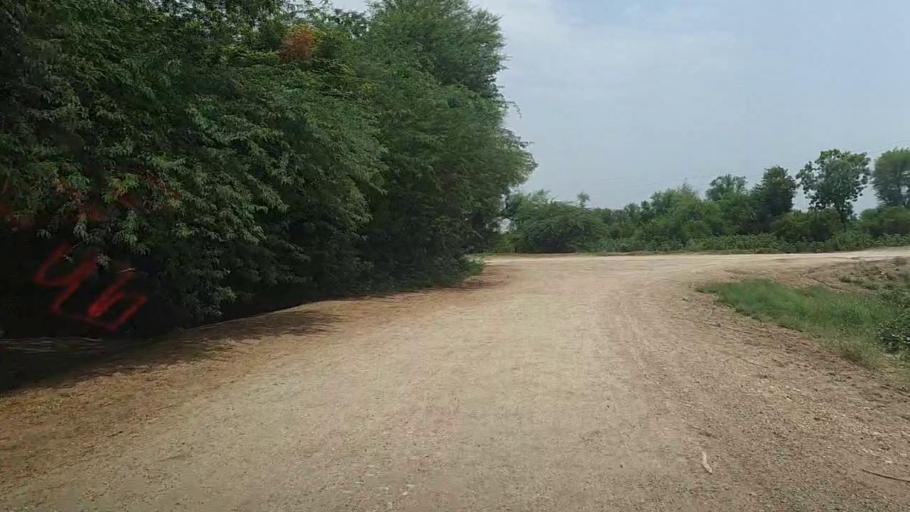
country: PK
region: Sindh
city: Karaundi
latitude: 26.9065
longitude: 68.3218
